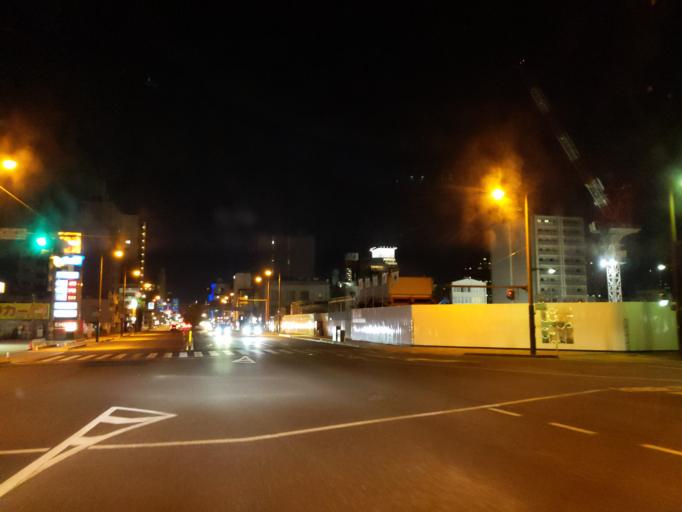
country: JP
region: Okayama
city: Okayama-shi
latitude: 34.6563
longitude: 133.9305
